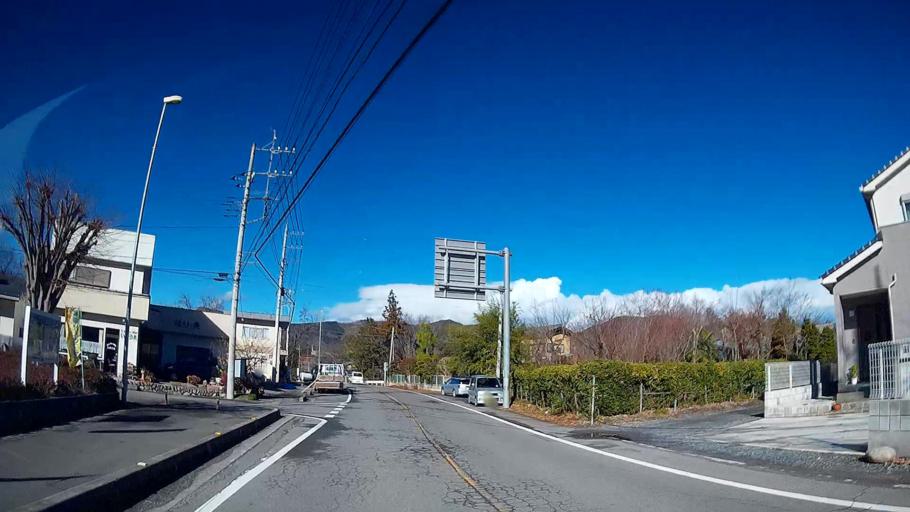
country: JP
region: Saitama
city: Kodamacho-kodamaminami
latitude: 36.1098
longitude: 139.1178
